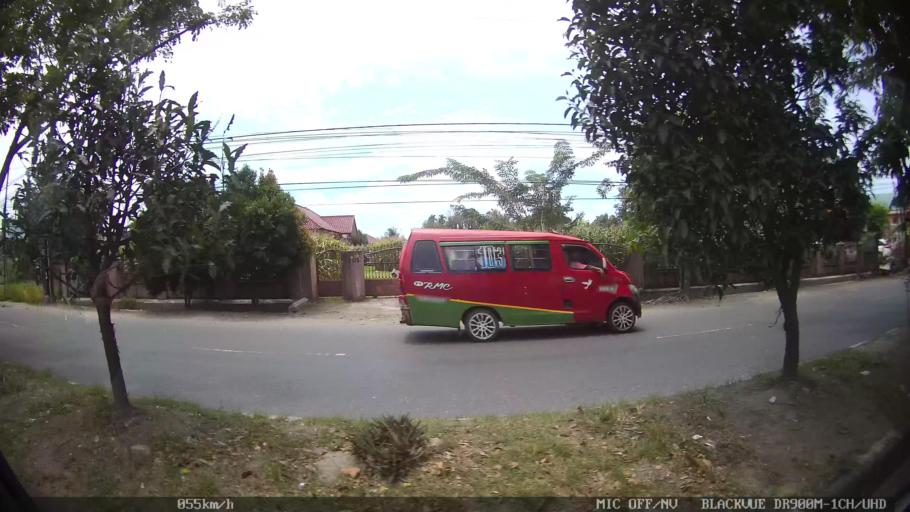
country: ID
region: North Sumatra
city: Sunggal
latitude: 3.5242
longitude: 98.6287
